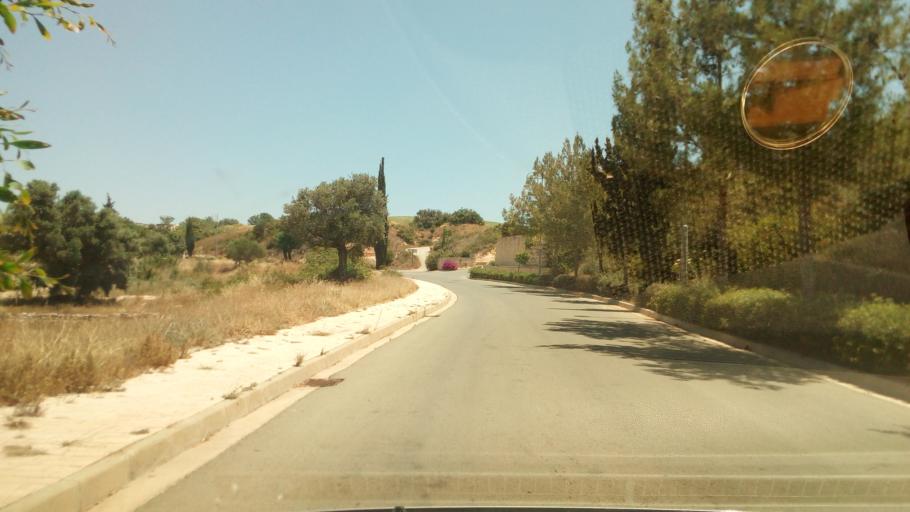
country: CY
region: Limassol
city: Pissouri
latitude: 34.6874
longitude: 32.6054
